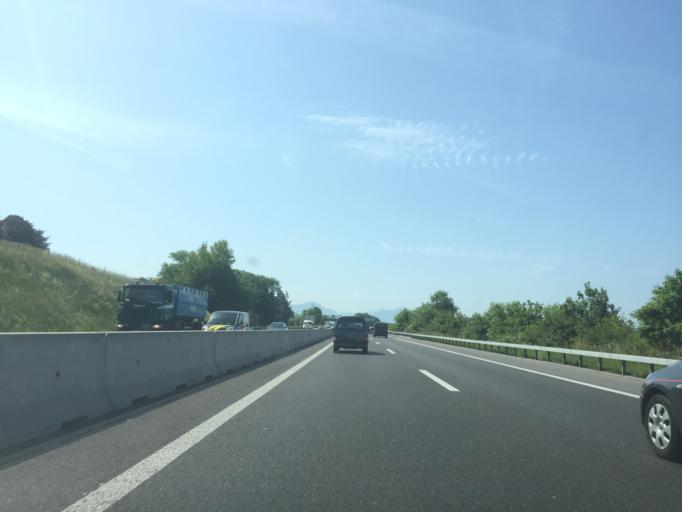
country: CH
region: Vaud
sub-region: Ouest Lausannois District
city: Bussigny
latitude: 46.5736
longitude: 6.5567
